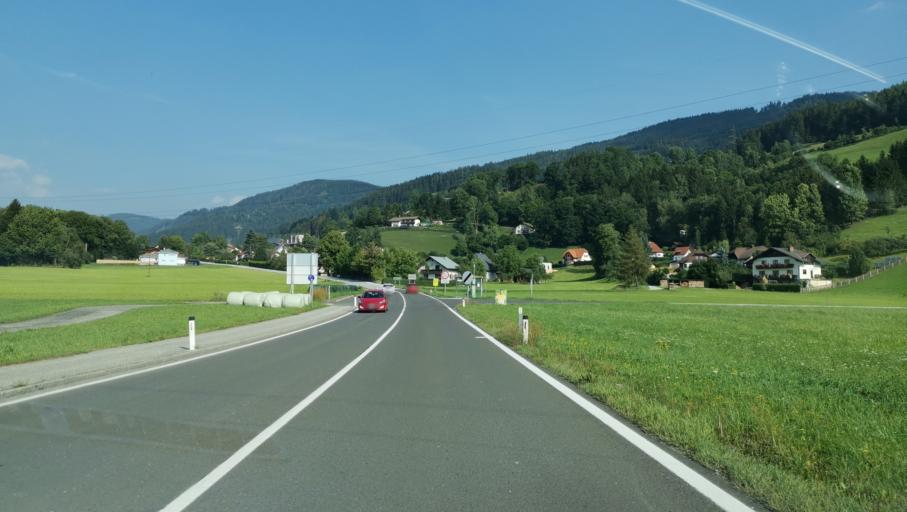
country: AT
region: Styria
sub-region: Politischer Bezirk Liezen
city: Trieben
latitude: 47.4991
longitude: 14.4829
